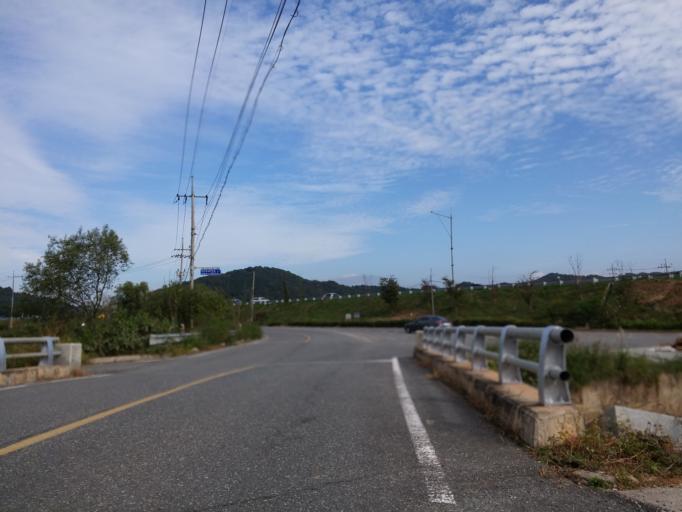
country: KR
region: Chungcheongnam-do
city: Yonmu
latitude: 36.1612
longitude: 127.1777
